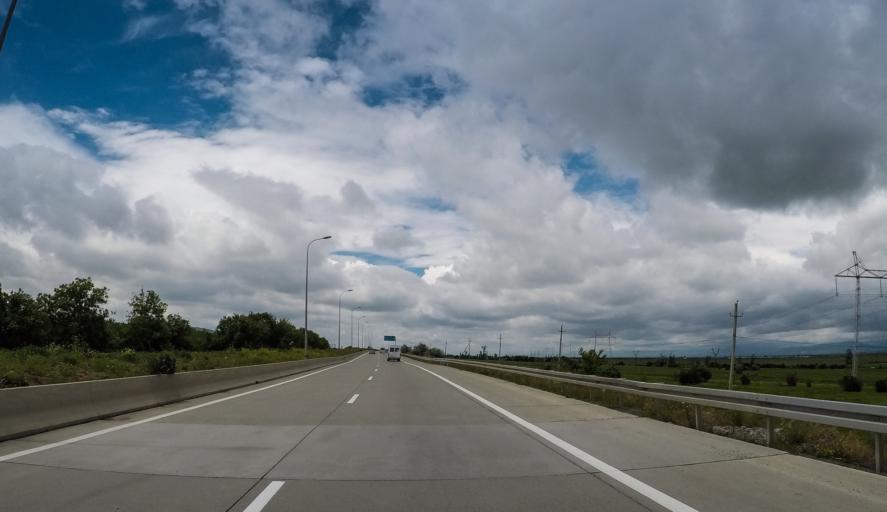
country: GE
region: Shida Kartli
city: Kaspi
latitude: 42.0202
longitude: 44.3084
